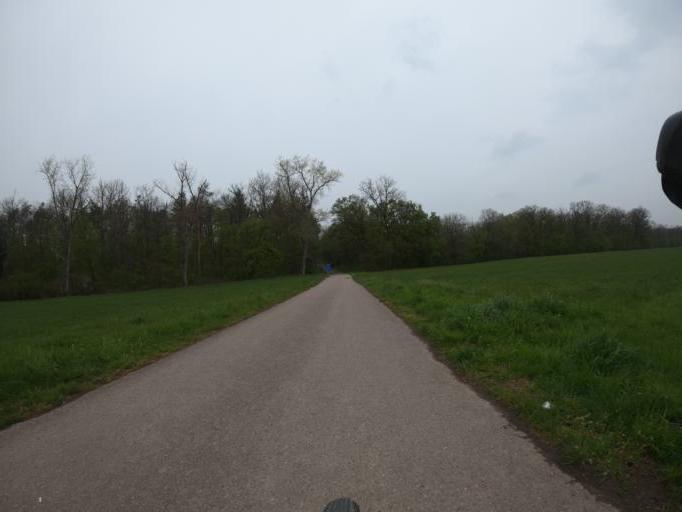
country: DE
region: Baden-Wuerttemberg
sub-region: Karlsruhe Region
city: Illingen
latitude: 48.9656
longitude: 8.9232
